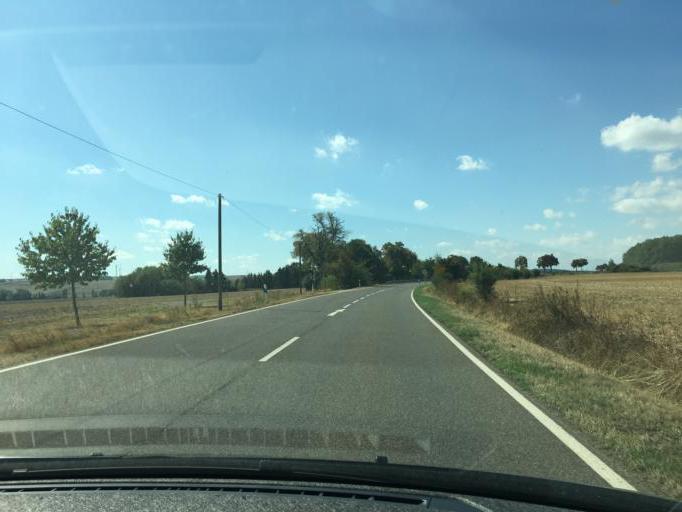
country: DE
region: North Rhine-Westphalia
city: Zulpich
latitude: 50.6712
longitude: 6.6015
